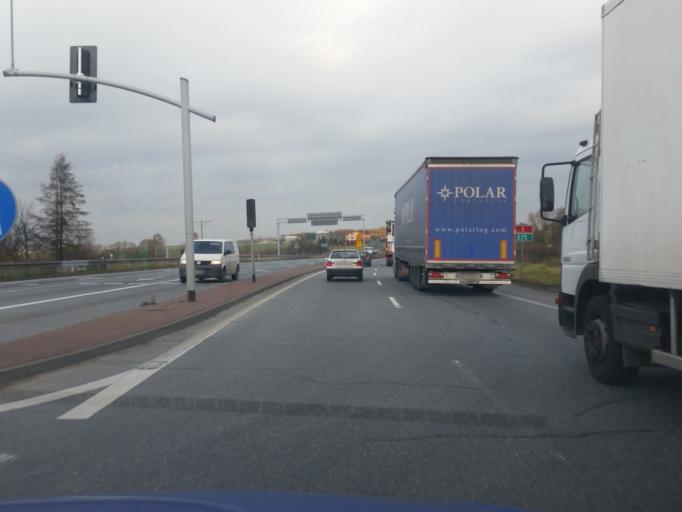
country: PL
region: Silesian Voivodeship
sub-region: Powiat myszkowski
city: Kozieglowy
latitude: 50.5982
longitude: 19.1496
